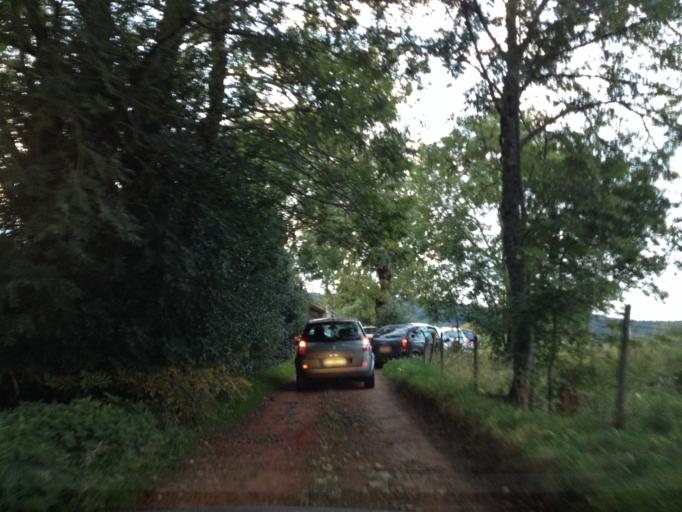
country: FR
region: Rhone-Alpes
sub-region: Departement de la Loire
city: Saint-Just-en-Chevalet
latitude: 45.9747
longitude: 3.8796
